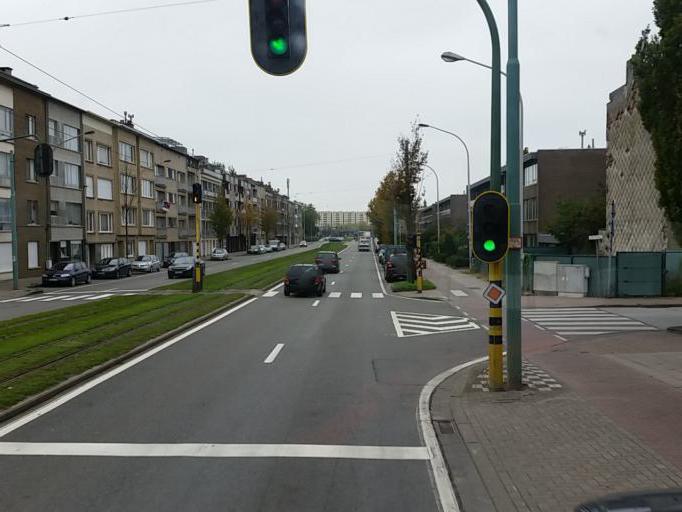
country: BE
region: Flanders
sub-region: Provincie Antwerpen
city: Antwerpen
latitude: 51.2414
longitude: 4.4347
